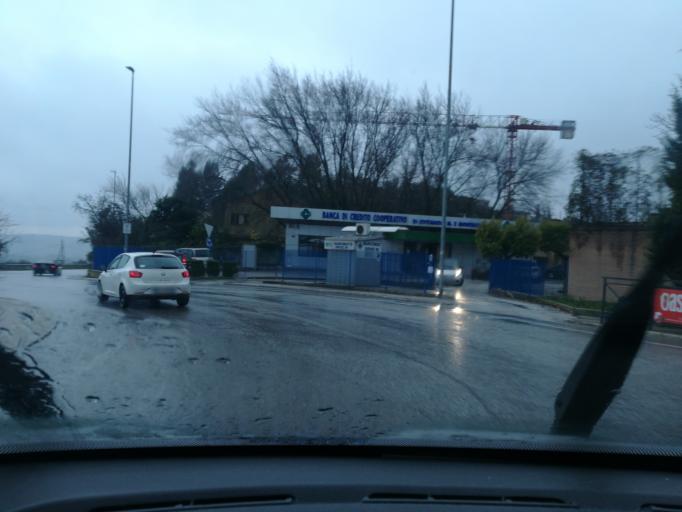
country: IT
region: The Marches
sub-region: Provincia di Macerata
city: Macerata
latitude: 43.2884
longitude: 13.4348
